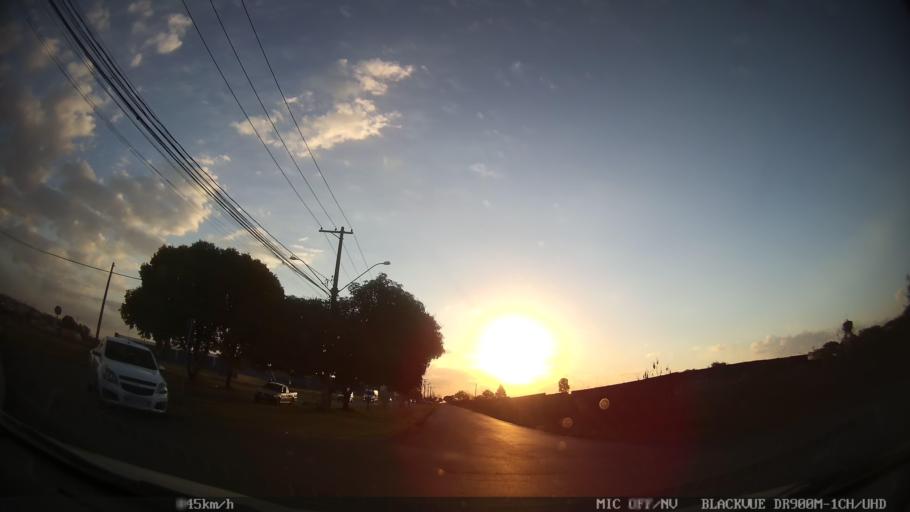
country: BR
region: Sao Paulo
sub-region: Ribeirao Preto
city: Ribeirao Preto
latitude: -21.1519
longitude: -47.7619
